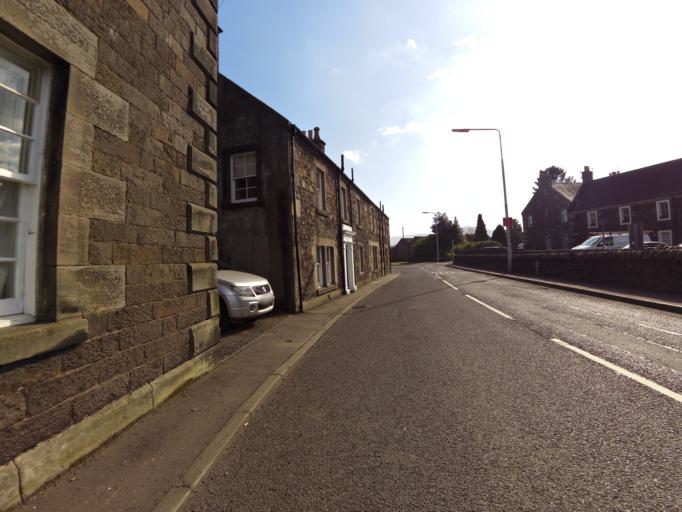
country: GB
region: Scotland
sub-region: Fife
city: Auchtermuchty
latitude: 56.2907
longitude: -3.2292
